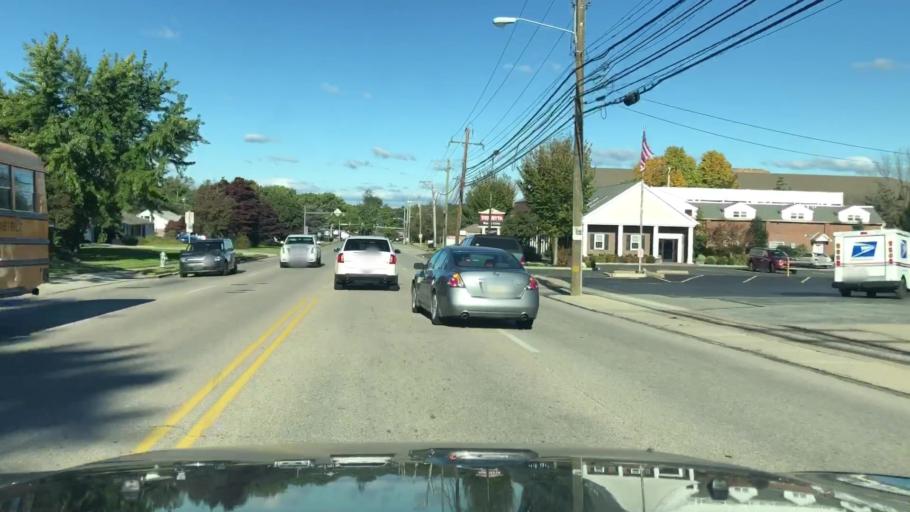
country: US
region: Pennsylvania
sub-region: Montgomery County
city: Plymouth Meeting
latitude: 40.1271
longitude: -75.2969
